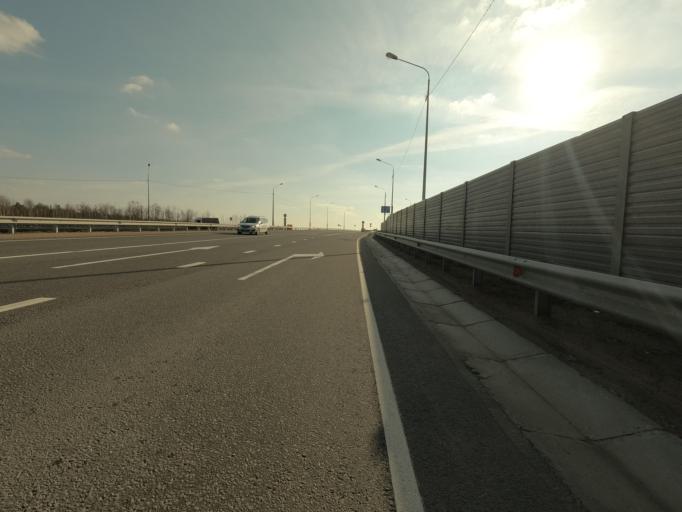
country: RU
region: Leningrad
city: Mga
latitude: 59.7586
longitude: 31.0935
